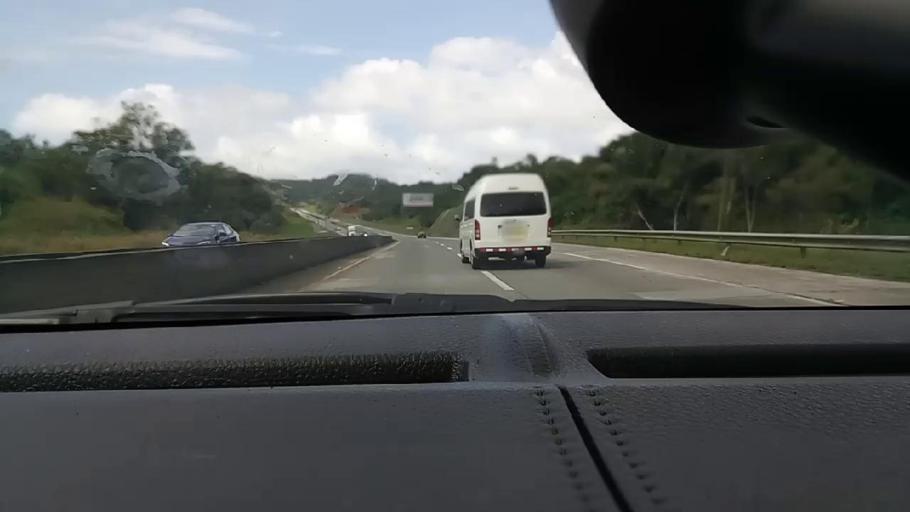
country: PA
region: Colon
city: Gatun
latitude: 9.2814
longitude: -79.7638
